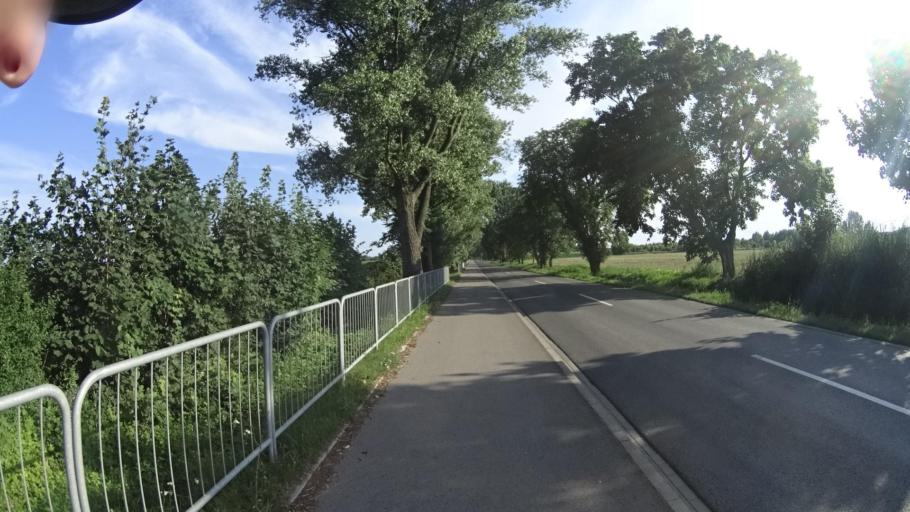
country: PL
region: Masovian Voivodeship
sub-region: Powiat pruszkowski
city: Nadarzyn
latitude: 52.0585
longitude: 20.7857
